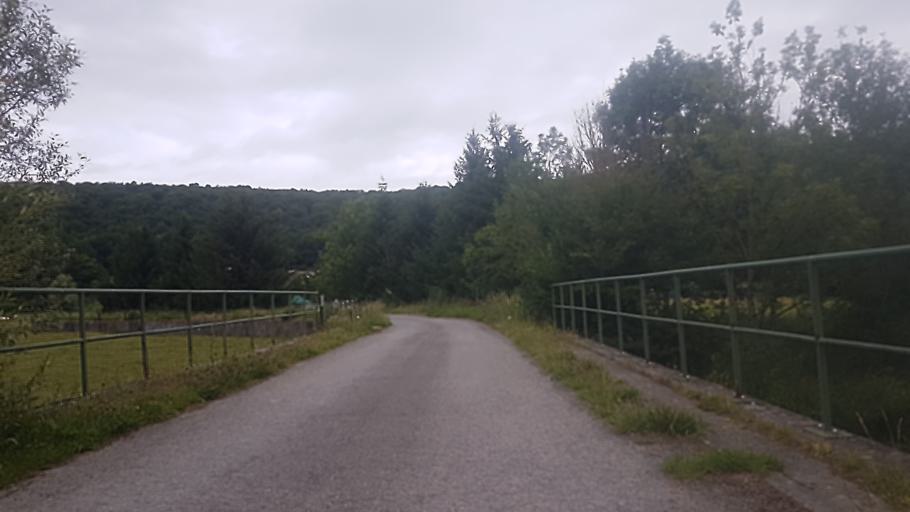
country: BE
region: Wallonia
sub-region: Province de Namur
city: Couvin
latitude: 50.0855
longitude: 4.5565
